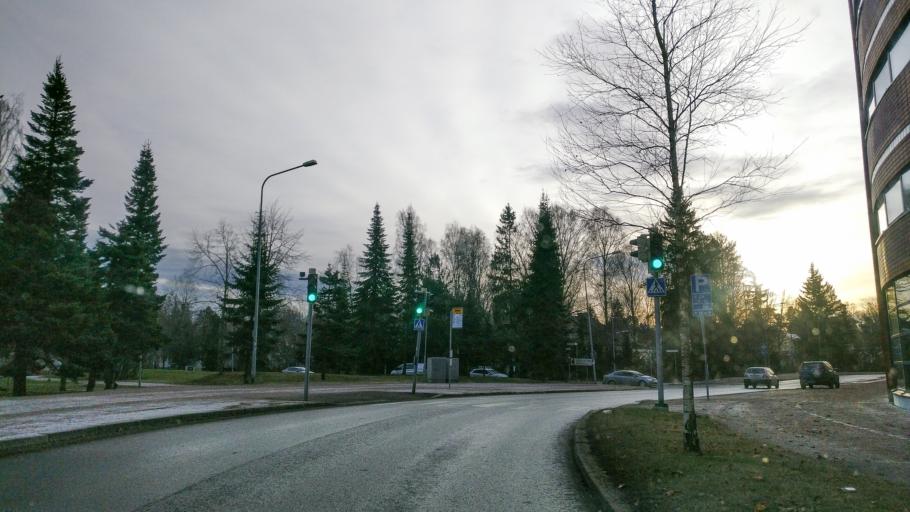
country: FI
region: Uusimaa
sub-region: Helsinki
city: Vantaa
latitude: 60.2050
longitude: 25.0765
